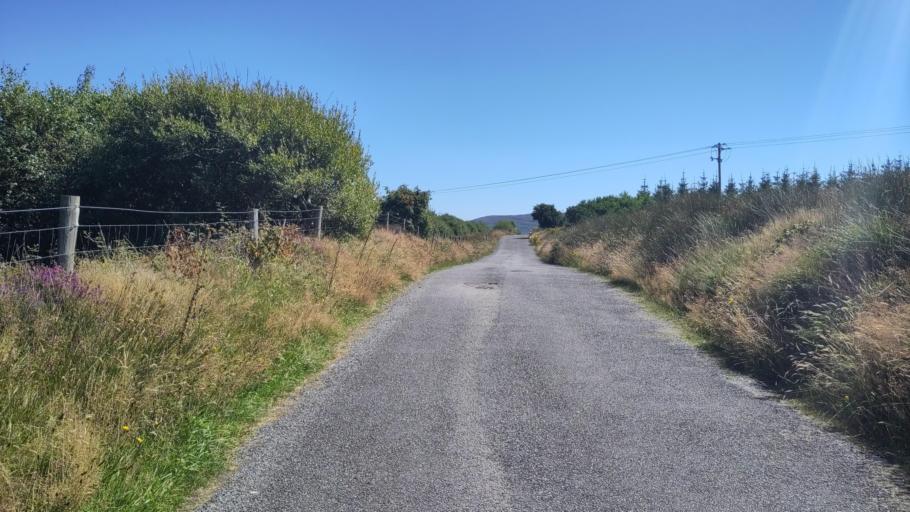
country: IE
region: Munster
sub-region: Ciarrai
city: Kenmare
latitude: 51.6680
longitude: -9.9126
